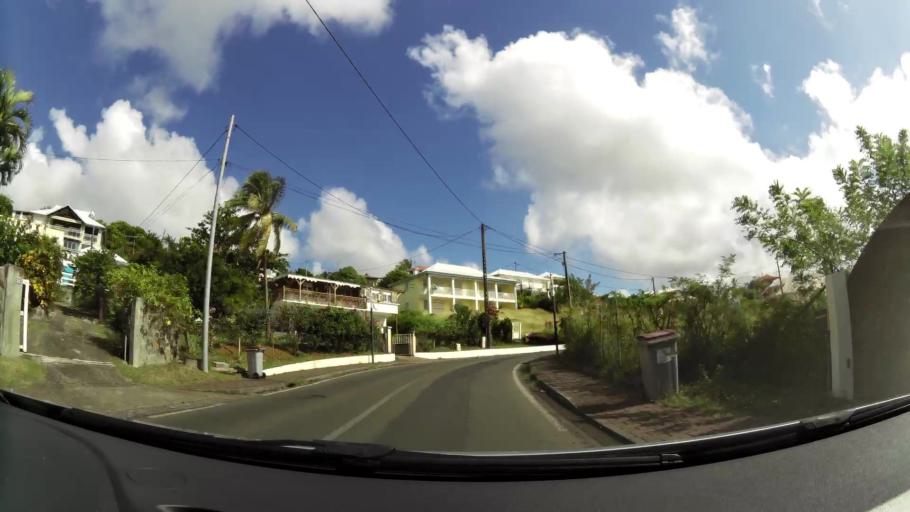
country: MQ
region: Martinique
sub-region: Martinique
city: Les Trois-Ilets
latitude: 14.4814
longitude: -61.0196
